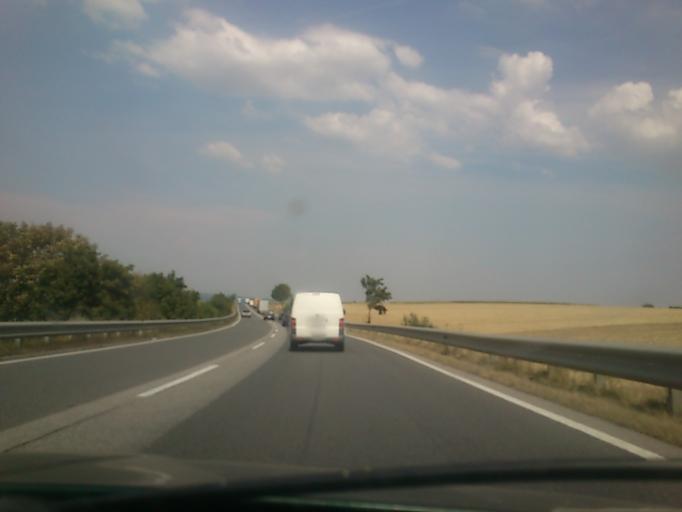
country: AT
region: Lower Austria
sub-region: Politischer Bezirk Mistelbach
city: Herrnbaumgarten
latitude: 48.7086
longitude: 16.6530
